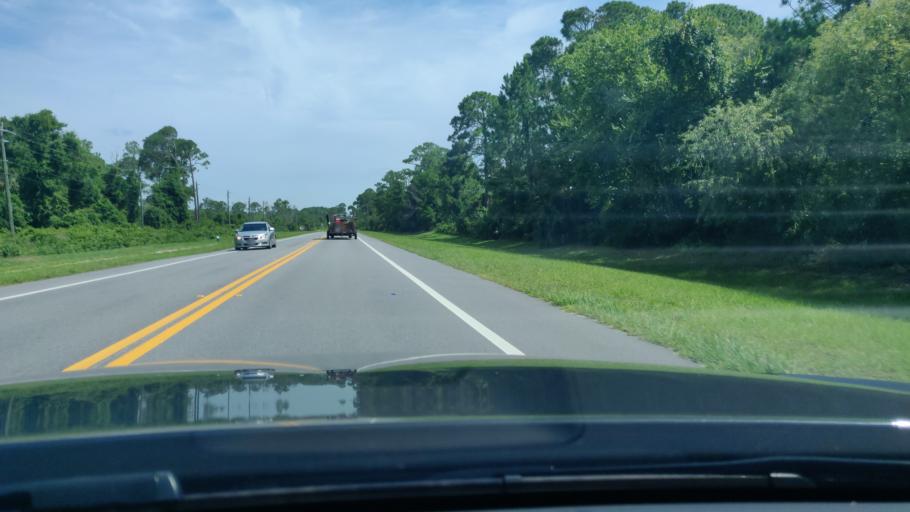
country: US
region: Florida
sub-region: Flagler County
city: Palm Coast
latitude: 29.5387
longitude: -81.1744
